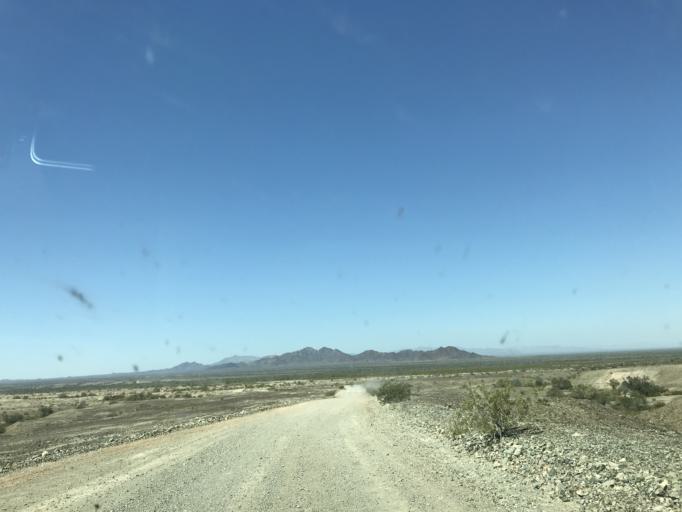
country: US
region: California
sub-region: Riverside County
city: Mesa Verde
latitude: 33.5006
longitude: -114.8556
